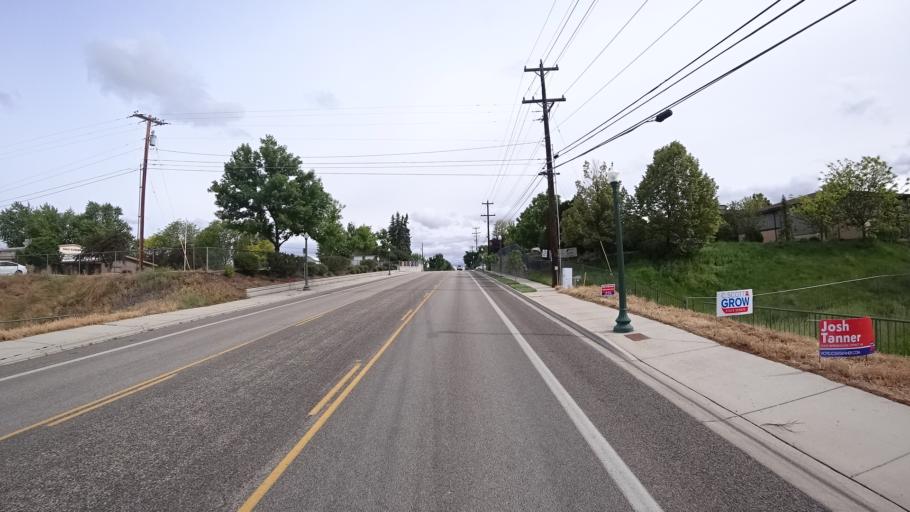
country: US
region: Idaho
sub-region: Ada County
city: Eagle
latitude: 43.6992
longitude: -116.3540
